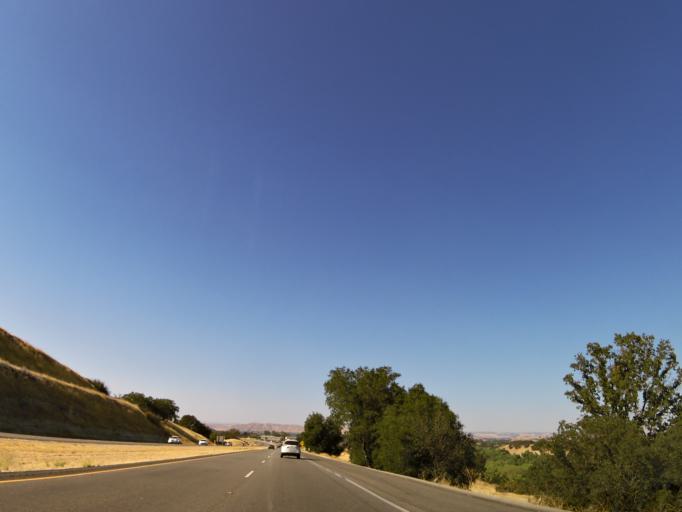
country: US
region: California
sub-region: San Luis Obispo County
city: Paso Robles
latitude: 35.6600
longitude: -120.6979
